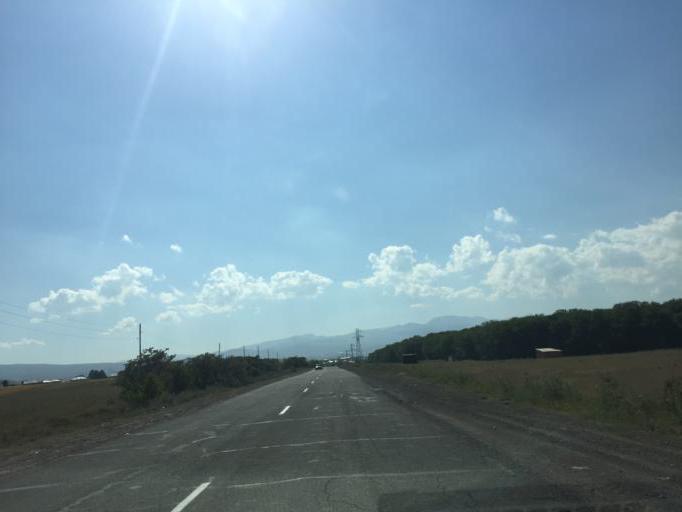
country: AM
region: Geghark'unik'i Marz
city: Vaghashen
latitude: 40.1456
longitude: 45.3402
